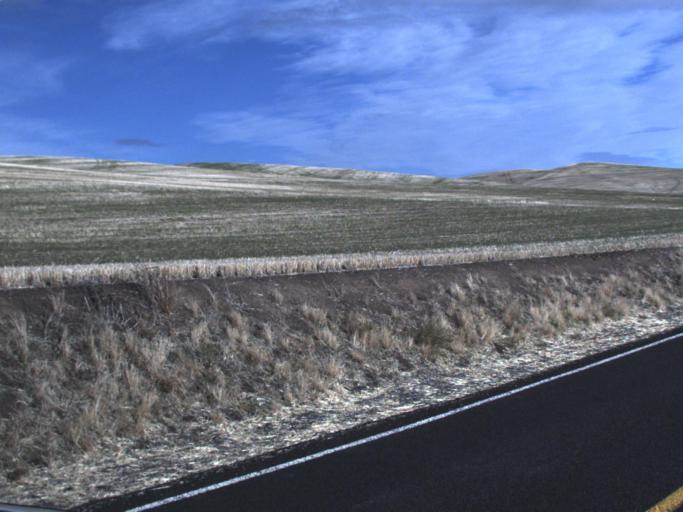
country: US
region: Washington
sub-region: Whitman County
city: Colfax
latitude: 46.9376
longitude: -117.1814
